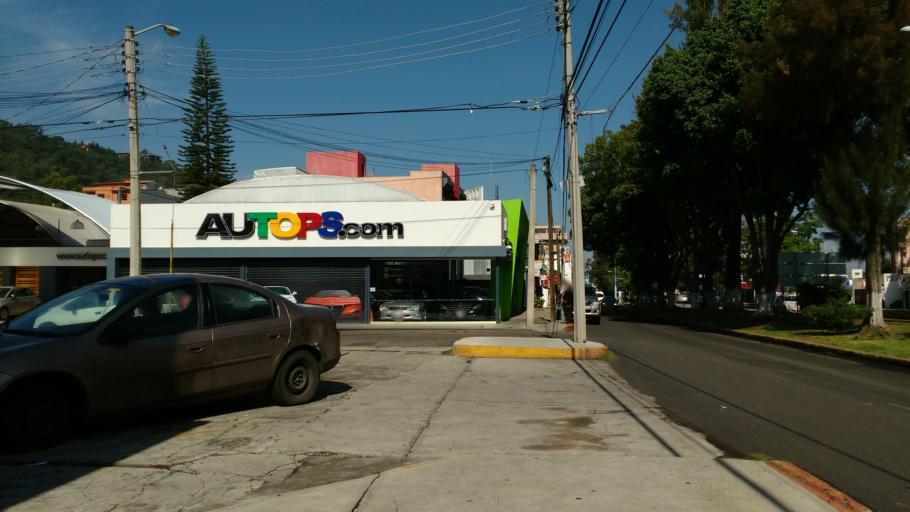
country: MX
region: Michoacan
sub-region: Morelia
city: Montana Monarca (Punta Altozano)
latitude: 19.6819
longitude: -101.1697
